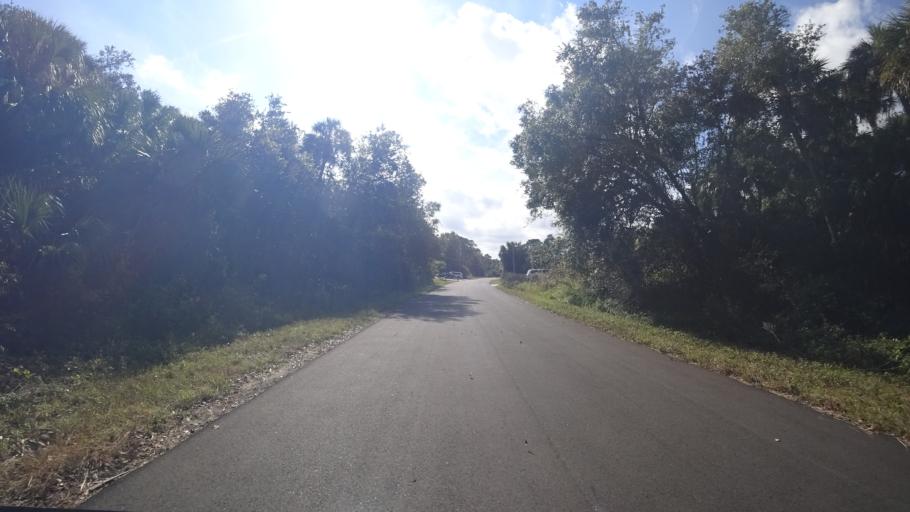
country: US
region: Florida
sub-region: Charlotte County
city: Port Charlotte
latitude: 27.0547
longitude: -82.1185
